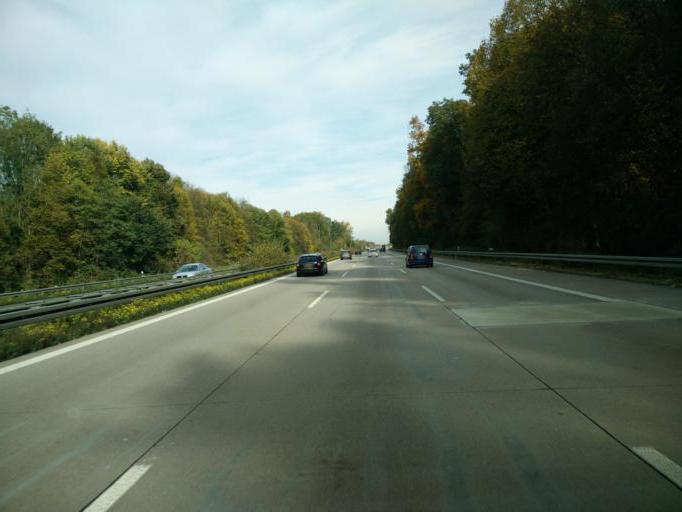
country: DE
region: Baden-Wuerttemberg
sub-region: Karlsruhe Region
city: Weingarten
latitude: 49.0442
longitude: 8.4902
